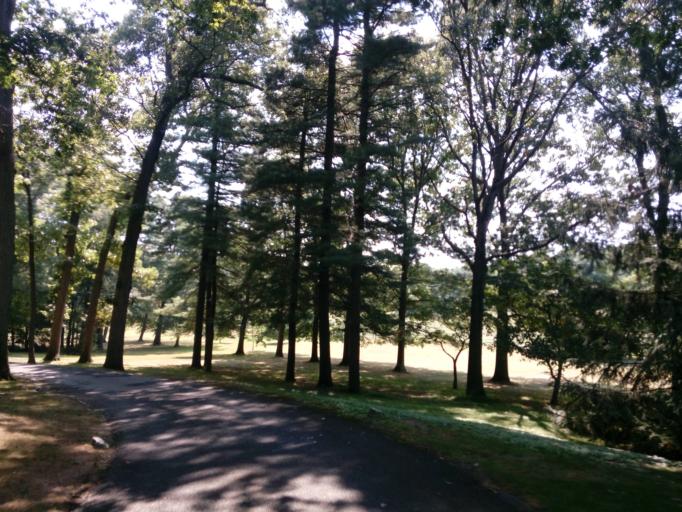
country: US
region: New York
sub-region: Nassau County
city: Locust Valley
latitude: 40.8608
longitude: -73.5954
